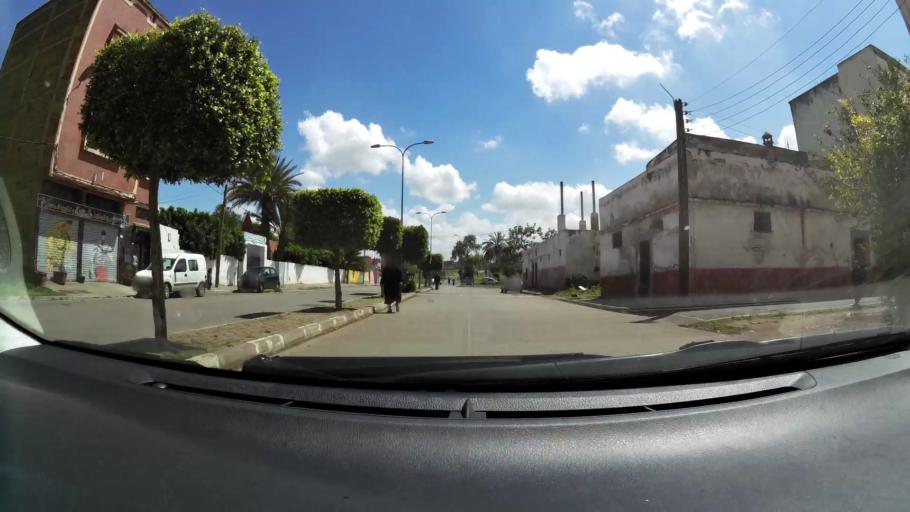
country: MA
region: Grand Casablanca
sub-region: Casablanca
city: Casablanca
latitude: 33.5611
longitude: -7.5801
